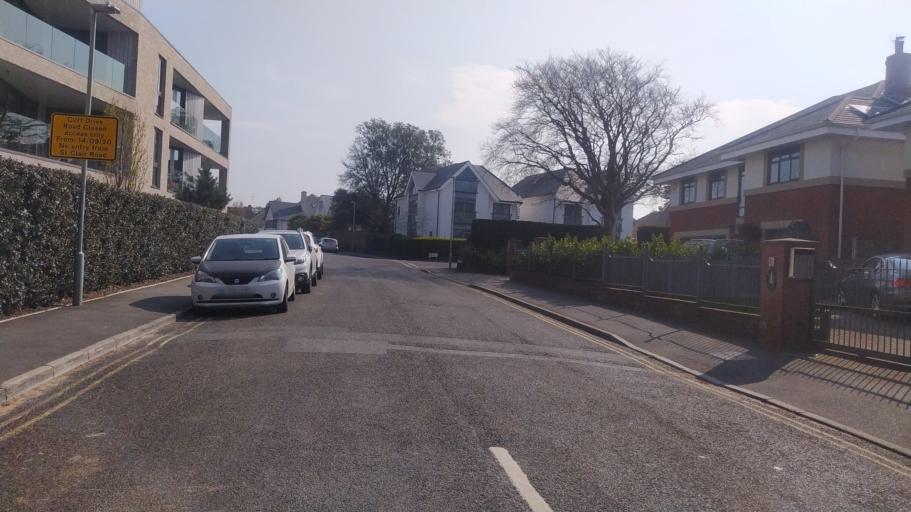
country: GB
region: England
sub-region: Dorset
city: Parkstone
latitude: 50.7010
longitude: -1.9259
